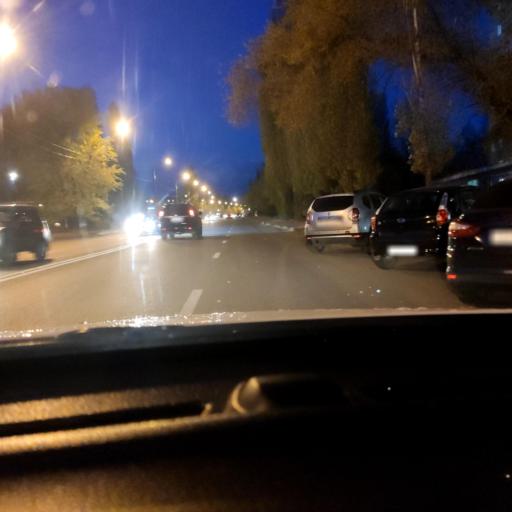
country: RU
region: Voronezj
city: Maslovka
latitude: 51.6348
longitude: 39.2636
